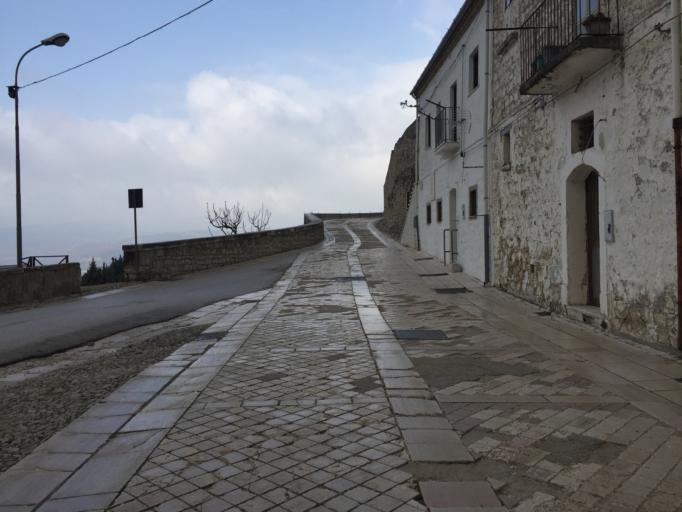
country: IT
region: Apulia
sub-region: Provincia di Foggia
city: Bovino
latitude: 41.2514
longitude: 15.3386
